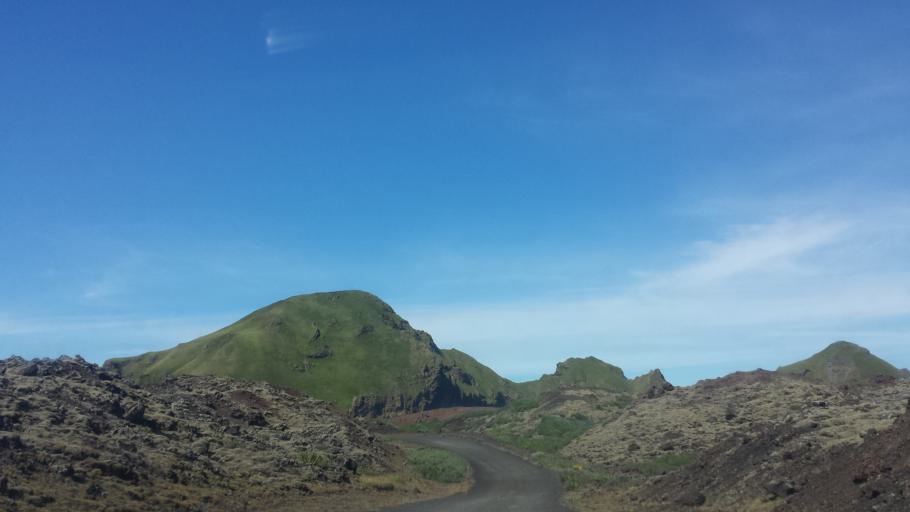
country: IS
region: South
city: Vestmannaeyjar
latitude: 63.4399
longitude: -20.2469
